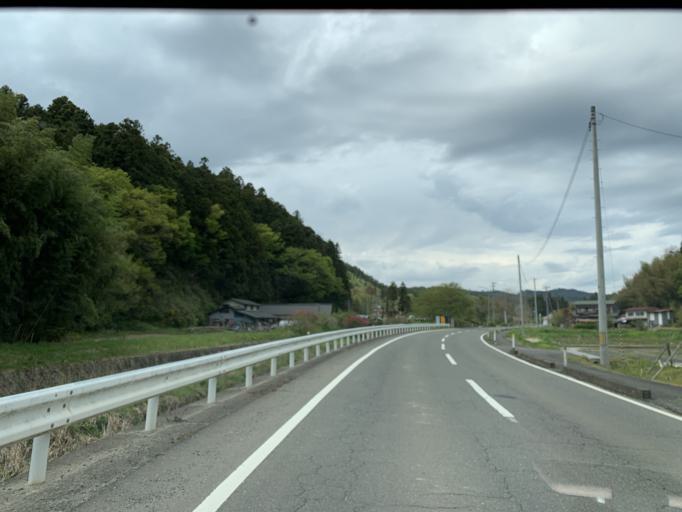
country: JP
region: Iwate
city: Ichinoseki
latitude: 38.7826
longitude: 141.3265
